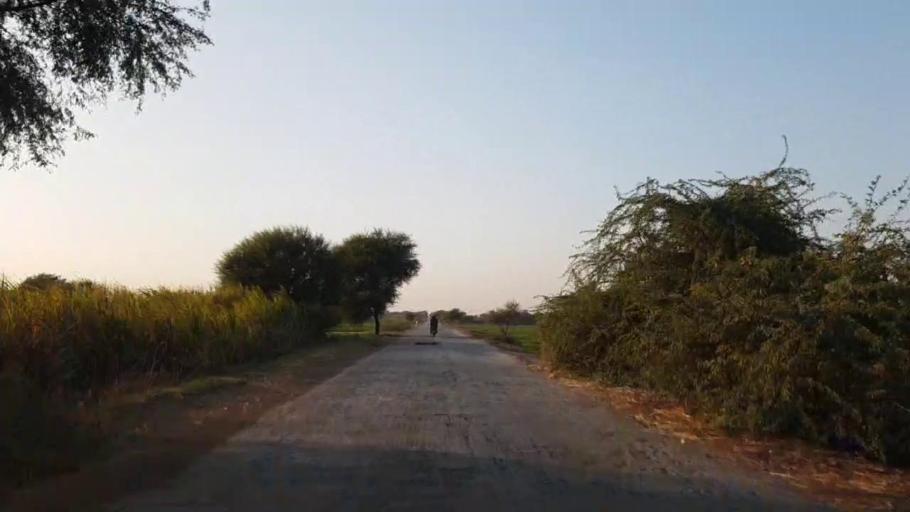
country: PK
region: Sindh
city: Chambar
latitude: 25.2303
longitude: 68.7068
